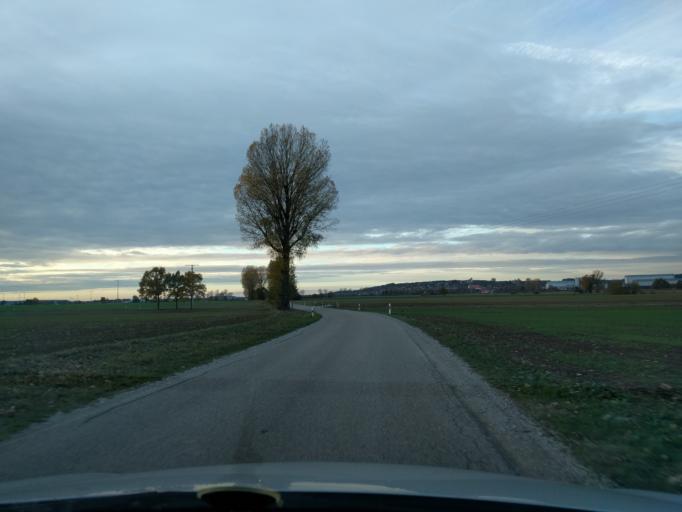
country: DE
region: Bavaria
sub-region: Regierungsbezirk Mittelfranken
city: Herrieden
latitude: 49.2160
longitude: 10.5090
